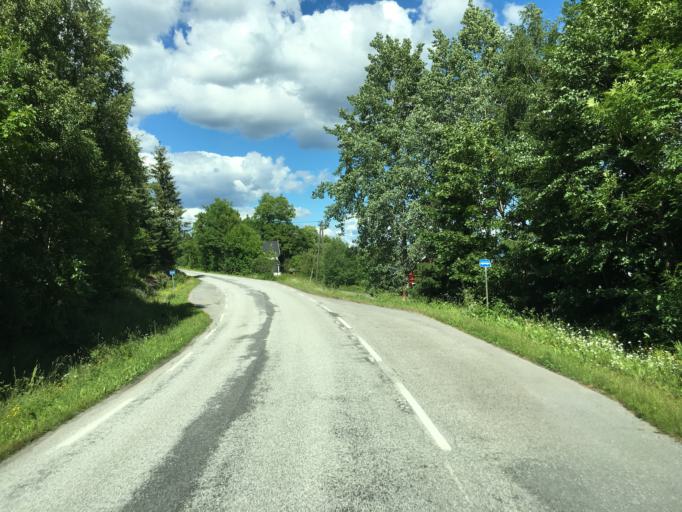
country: NO
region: Oppland
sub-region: Jevnaker
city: Jevnaker
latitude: 60.3394
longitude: 10.3581
